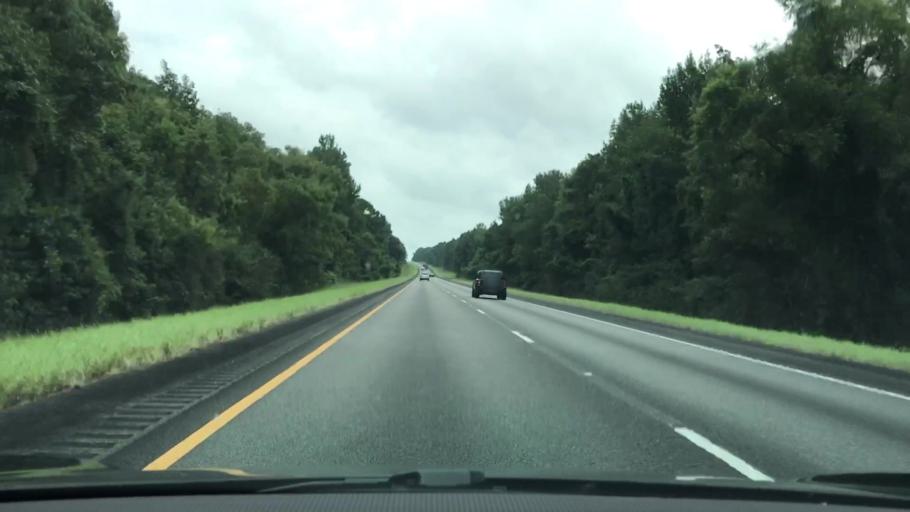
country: US
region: Alabama
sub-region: Elmore County
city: Tallassee
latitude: 32.4386
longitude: -85.8396
